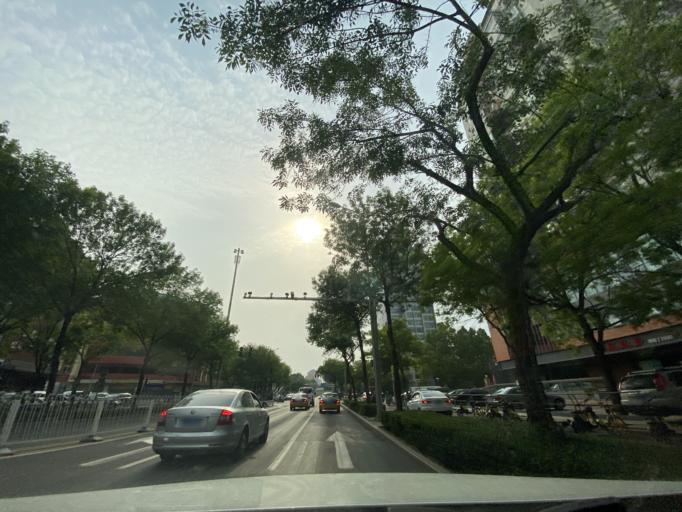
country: CN
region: Beijing
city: Haidian
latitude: 39.9752
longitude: 116.3401
